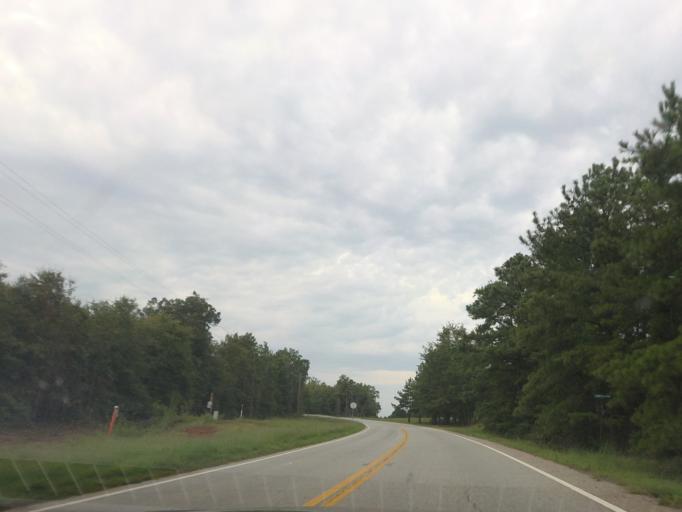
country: US
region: Georgia
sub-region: Twiggs County
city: Jeffersonville
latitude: 32.7584
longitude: -83.4439
